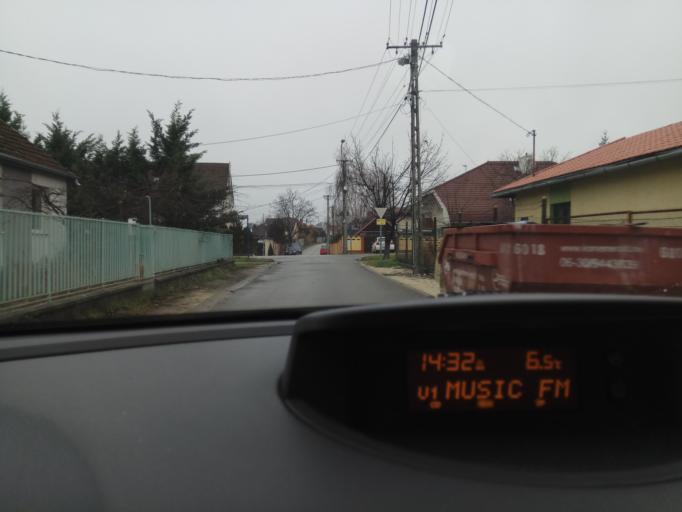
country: HU
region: Pest
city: Dunakeszi
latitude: 47.6072
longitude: 19.1299
